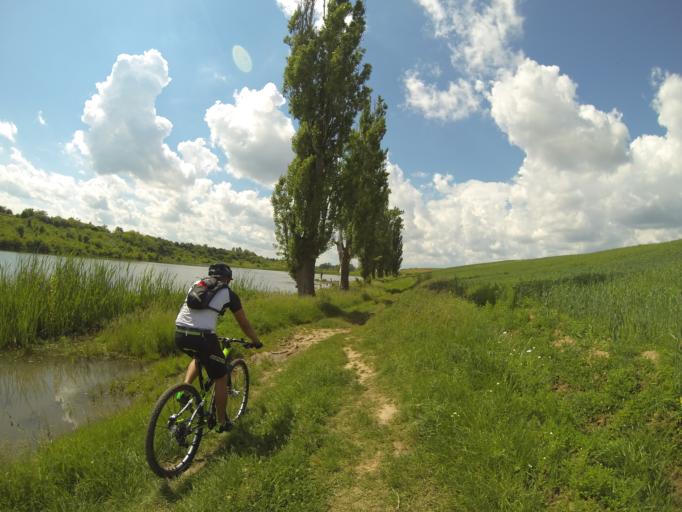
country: RO
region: Dolj
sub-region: Comuna Malu Mare
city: Preajba
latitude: 44.2669
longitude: 23.8540
